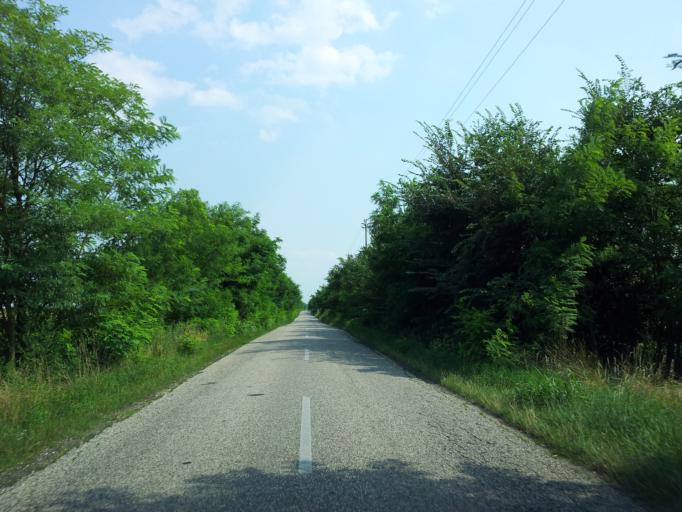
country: HU
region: Pest
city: Szigetujfalu
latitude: 47.2009
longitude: 18.9179
